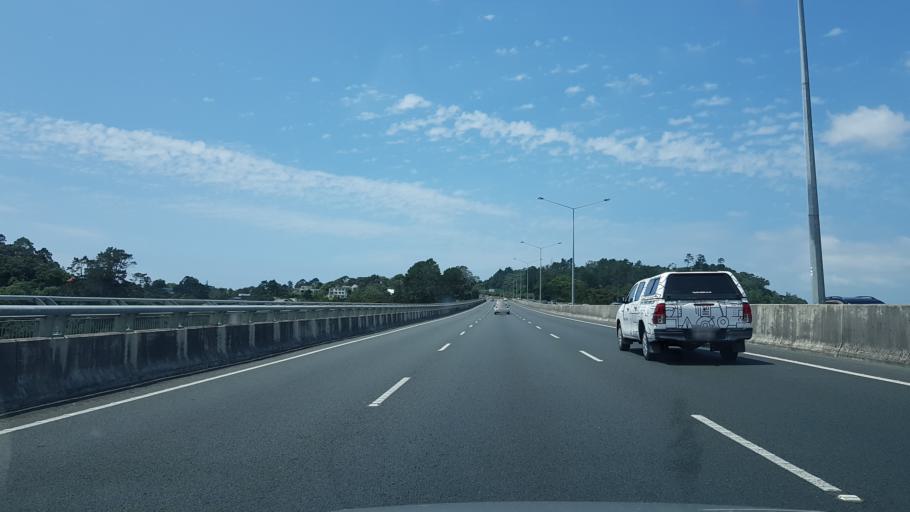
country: NZ
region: Auckland
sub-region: Auckland
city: North Shore
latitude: -36.7853
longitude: 174.6662
